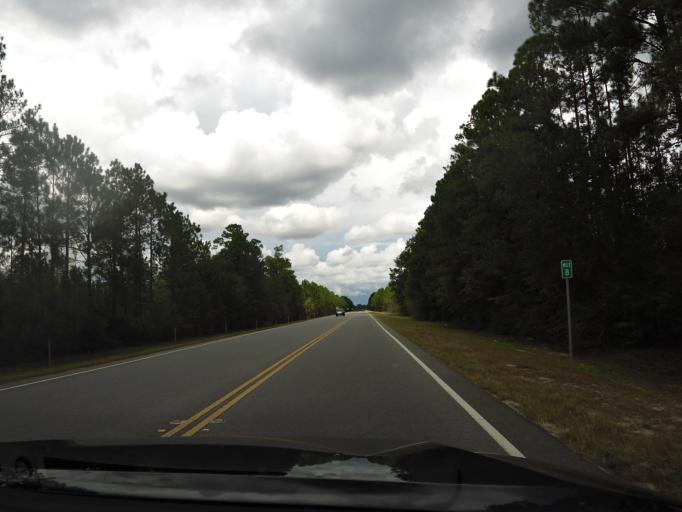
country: US
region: Georgia
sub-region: Brantley County
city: Nahunta
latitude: 31.1777
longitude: -81.9884
